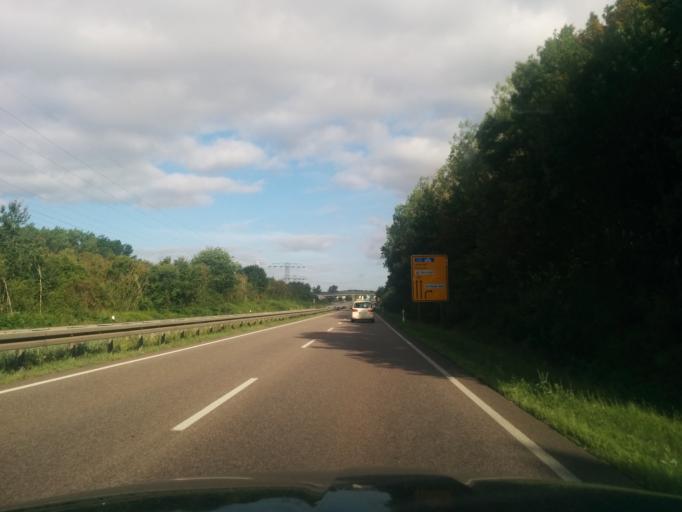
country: DE
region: Saxony-Anhalt
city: Angersdorf
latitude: 51.4687
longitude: 11.9119
